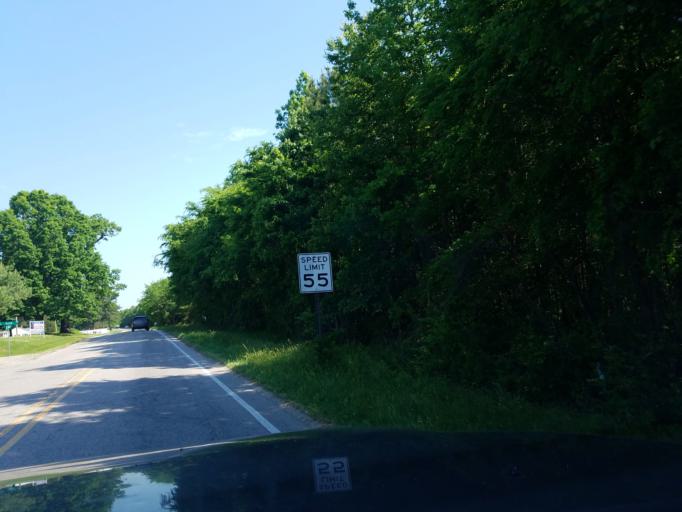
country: US
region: North Carolina
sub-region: Vance County
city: Henderson
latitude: 36.3412
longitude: -78.4474
